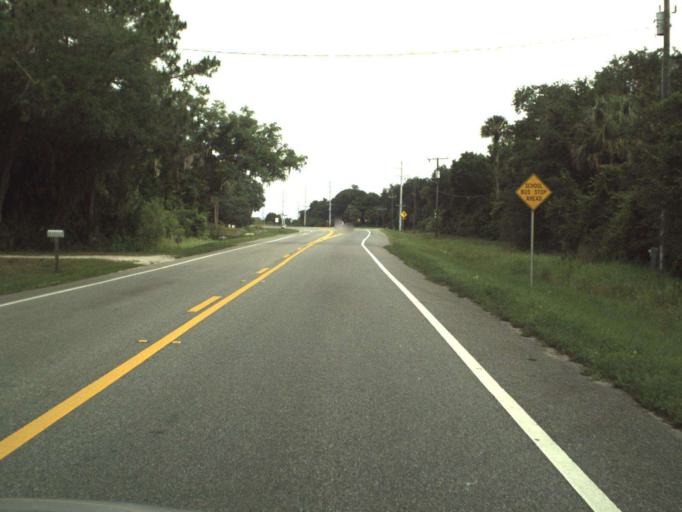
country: US
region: Florida
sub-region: Seminole County
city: Geneva
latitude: 28.7784
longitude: -81.1653
